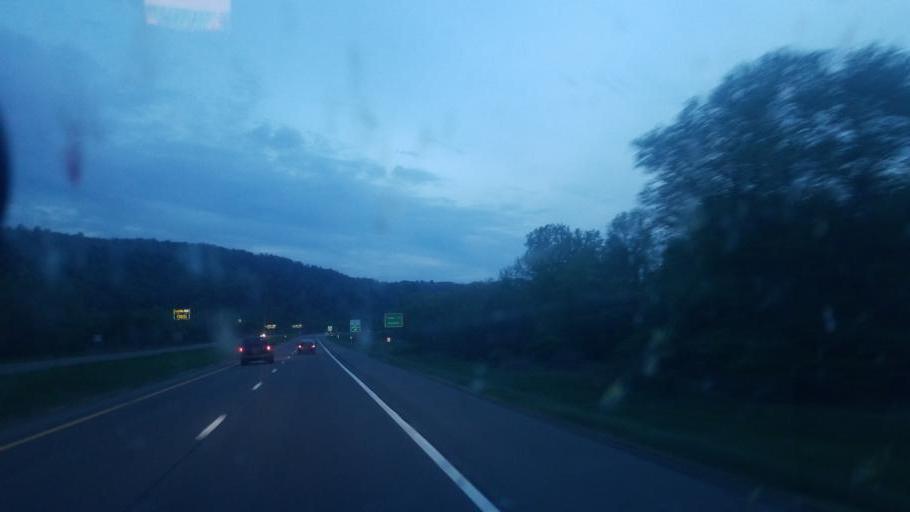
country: US
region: New York
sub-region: Tioga County
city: Owego
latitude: 42.0903
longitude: -76.2722
